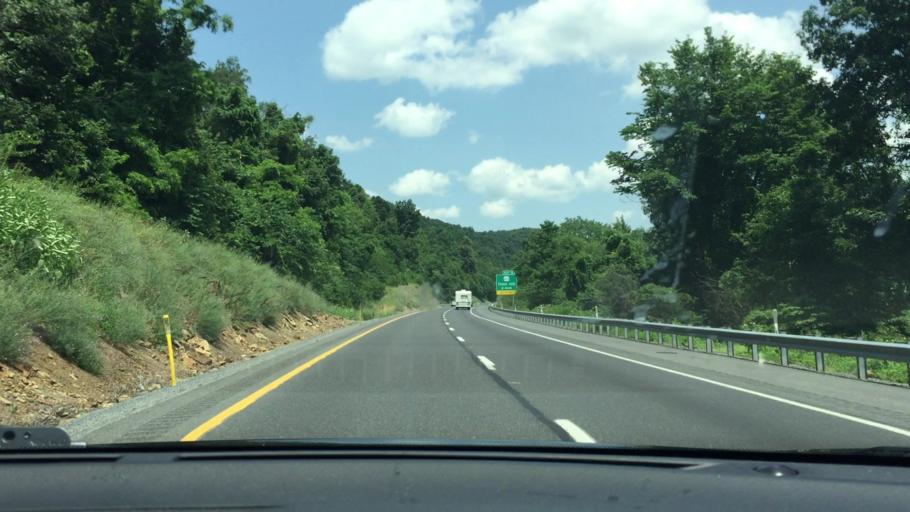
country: US
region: Pennsylvania
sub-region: Bedford County
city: Earlston
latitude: 39.8609
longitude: -78.2651
